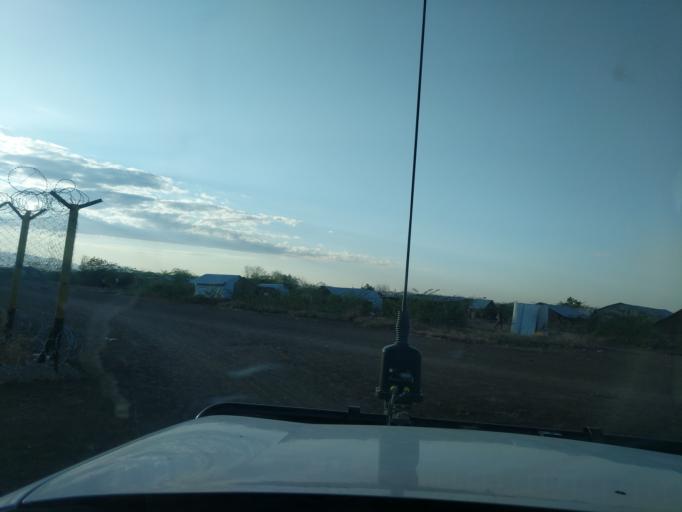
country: UG
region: Northern Region
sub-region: Kaabong District
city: Kaabong
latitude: 3.7569
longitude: 34.8104
